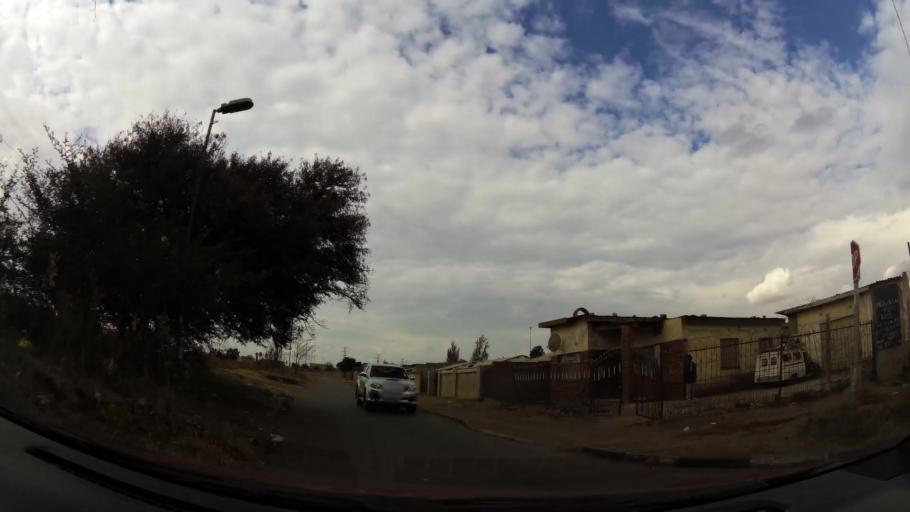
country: ZA
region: Gauteng
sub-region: City of Johannesburg Metropolitan Municipality
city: Soweto
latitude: -26.2419
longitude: 27.8496
